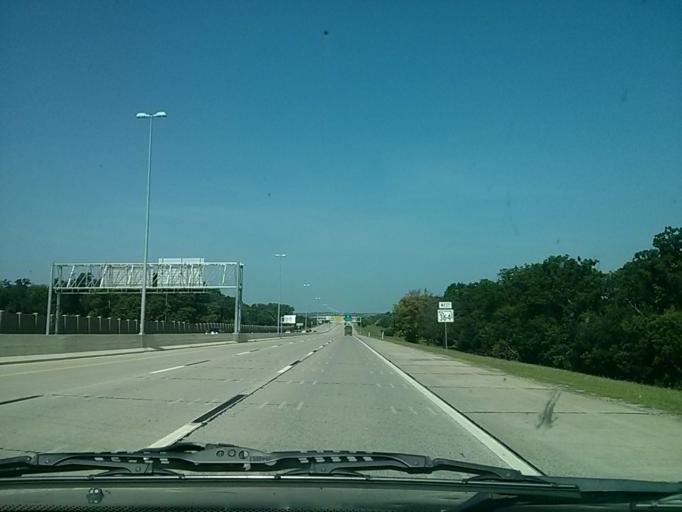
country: US
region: Oklahoma
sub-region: Tulsa County
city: Jenks
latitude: 36.0095
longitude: -95.9951
